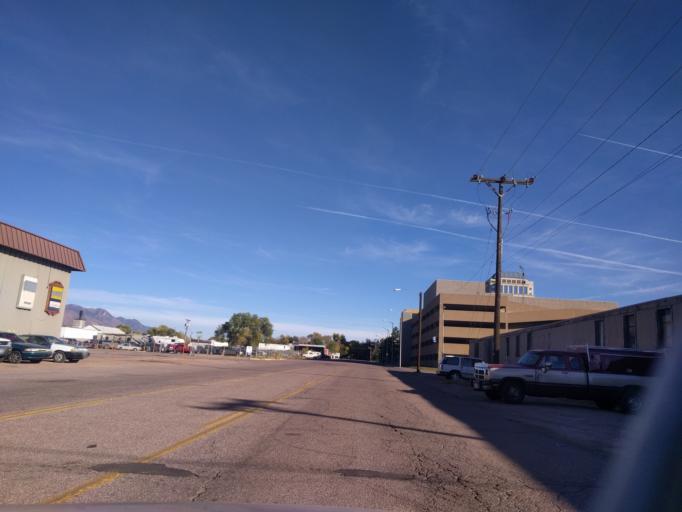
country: US
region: Colorado
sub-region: El Paso County
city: Colorado Springs
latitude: 38.8291
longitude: -104.8274
